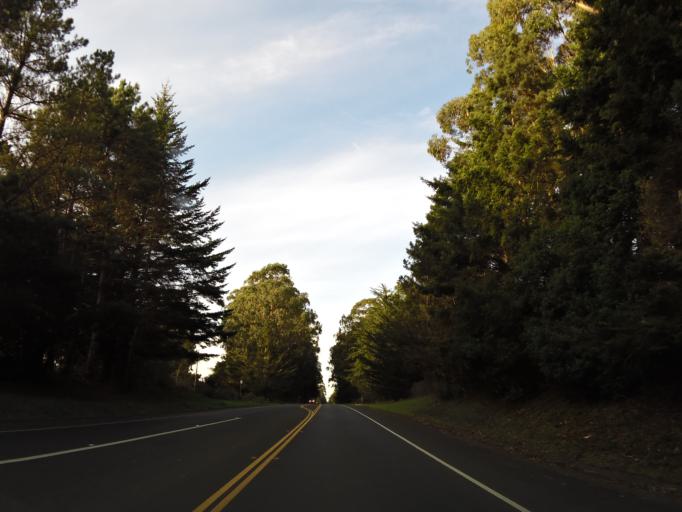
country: US
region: California
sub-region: Mendocino County
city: Fort Bragg
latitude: 39.3334
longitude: -123.8056
